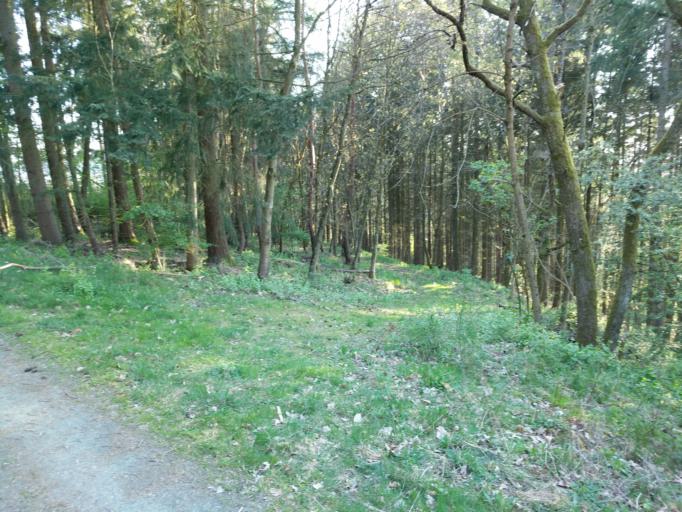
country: DE
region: Hesse
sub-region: Regierungsbezirk Giessen
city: Bad Endbach
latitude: 50.7596
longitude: 8.4846
